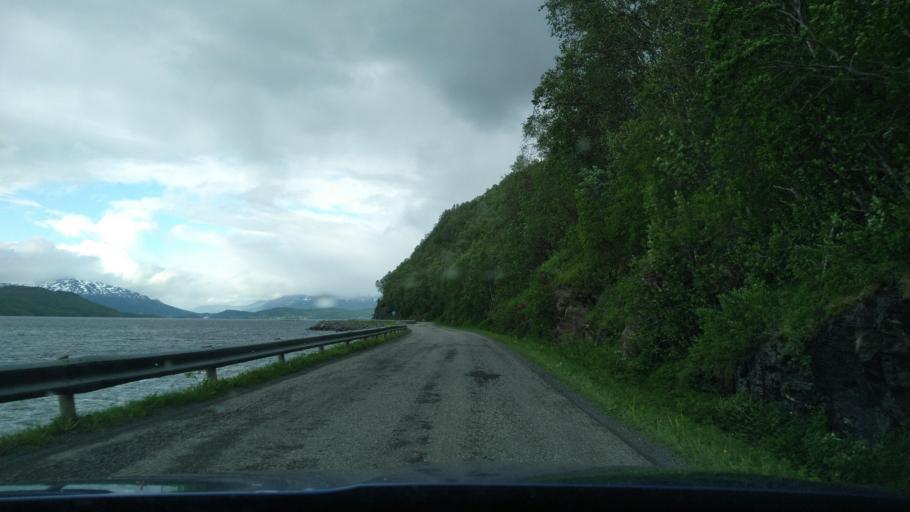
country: NO
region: Troms
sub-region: Lenvik
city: Finnsnes
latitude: 69.1422
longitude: 17.9167
